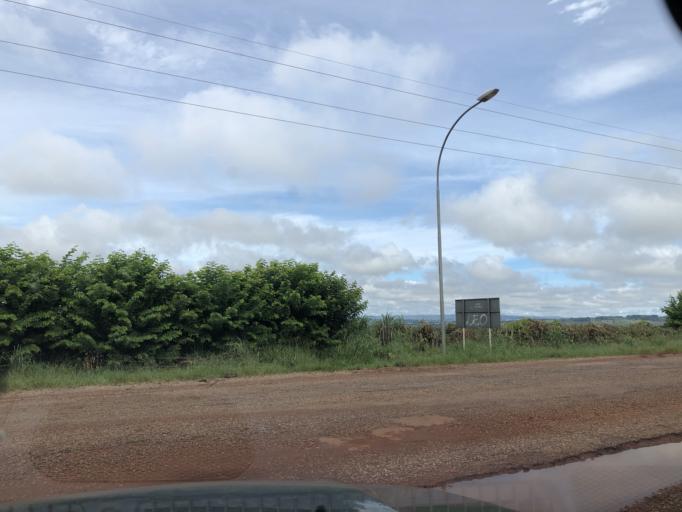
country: BR
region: Federal District
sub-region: Brasilia
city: Brasilia
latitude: -15.7590
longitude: -48.1273
